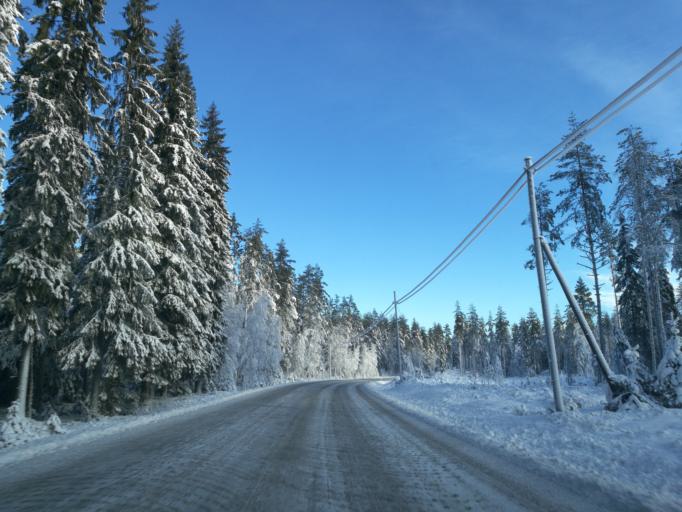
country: NO
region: Hedmark
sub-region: Grue
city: Kirkenaer
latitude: 60.4036
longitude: 12.3772
